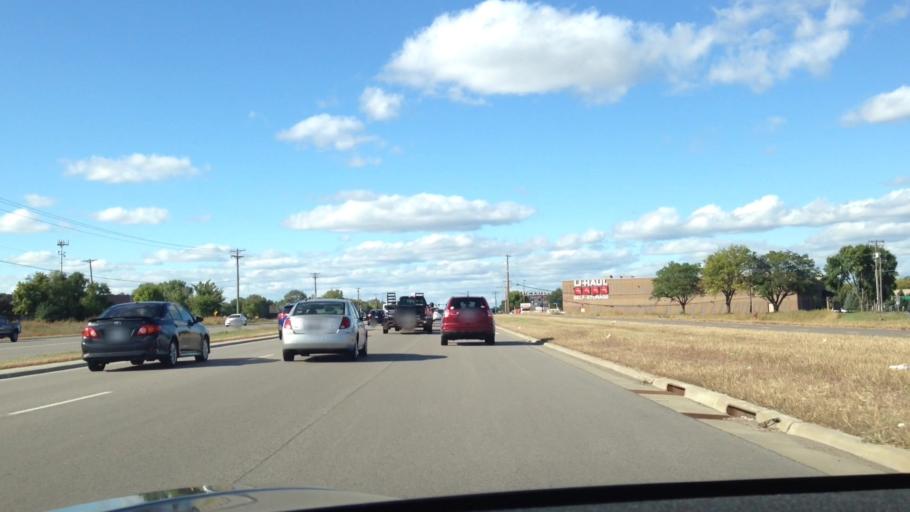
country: US
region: Minnesota
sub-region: Hennepin County
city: Brooklyn Park
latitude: 45.0801
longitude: -93.3748
